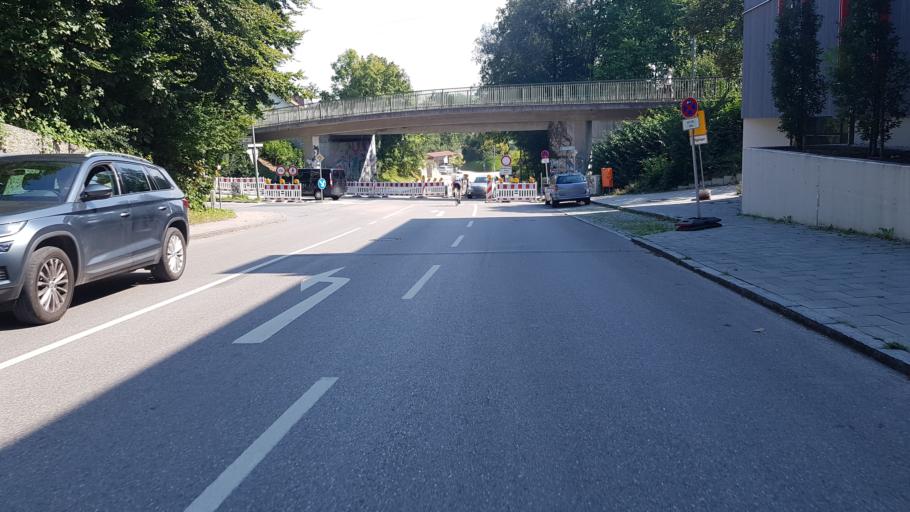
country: DE
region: Bavaria
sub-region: Upper Bavaria
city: Seefeld
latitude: 48.0392
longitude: 11.1954
